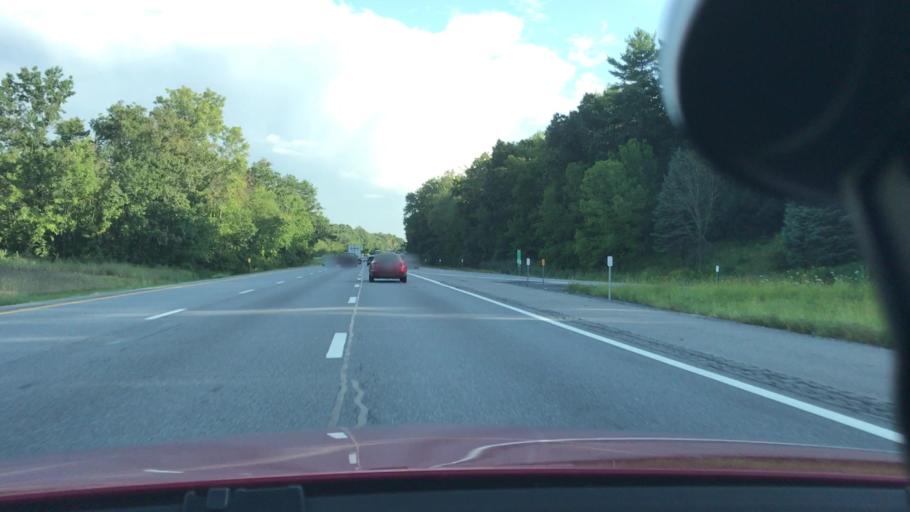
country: US
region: New York
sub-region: Saratoga County
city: Country Knolls
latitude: 42.8381
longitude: -73.7715
